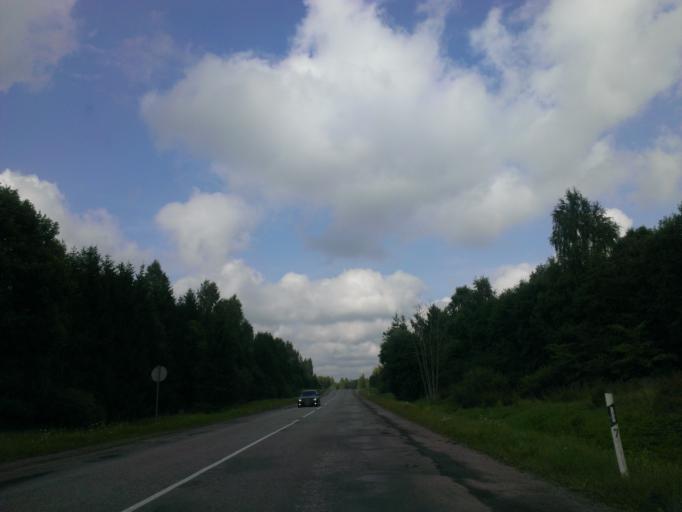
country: LV
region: Priekuli
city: Priekuli
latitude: 57.2730
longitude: 25.4750
